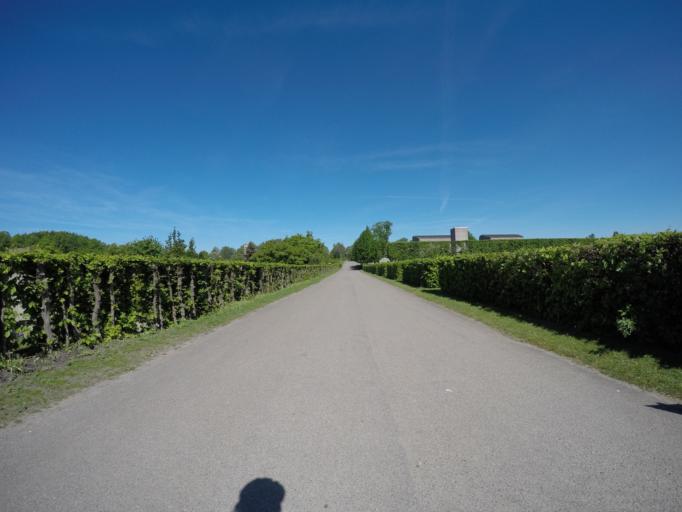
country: SE
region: Skane
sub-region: Malmo
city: Malmoe
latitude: 55.5919
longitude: 13.0425
